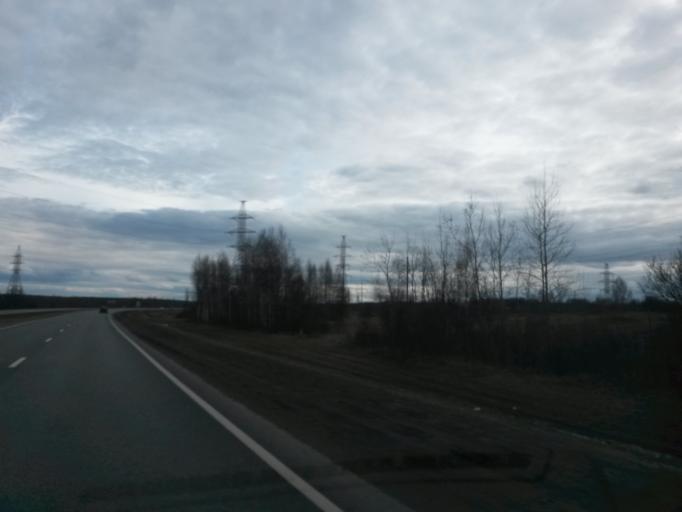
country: RU
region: Jaroslavl
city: Krasnyye Tkachi
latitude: 57.5186
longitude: 39.7866
